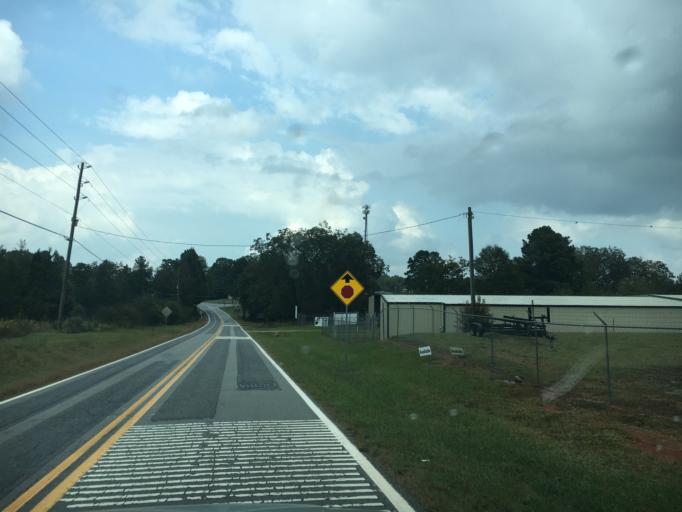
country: US
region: Georgia
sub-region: Hart County
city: Reed Creek
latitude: 34.4430
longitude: -82.9252
